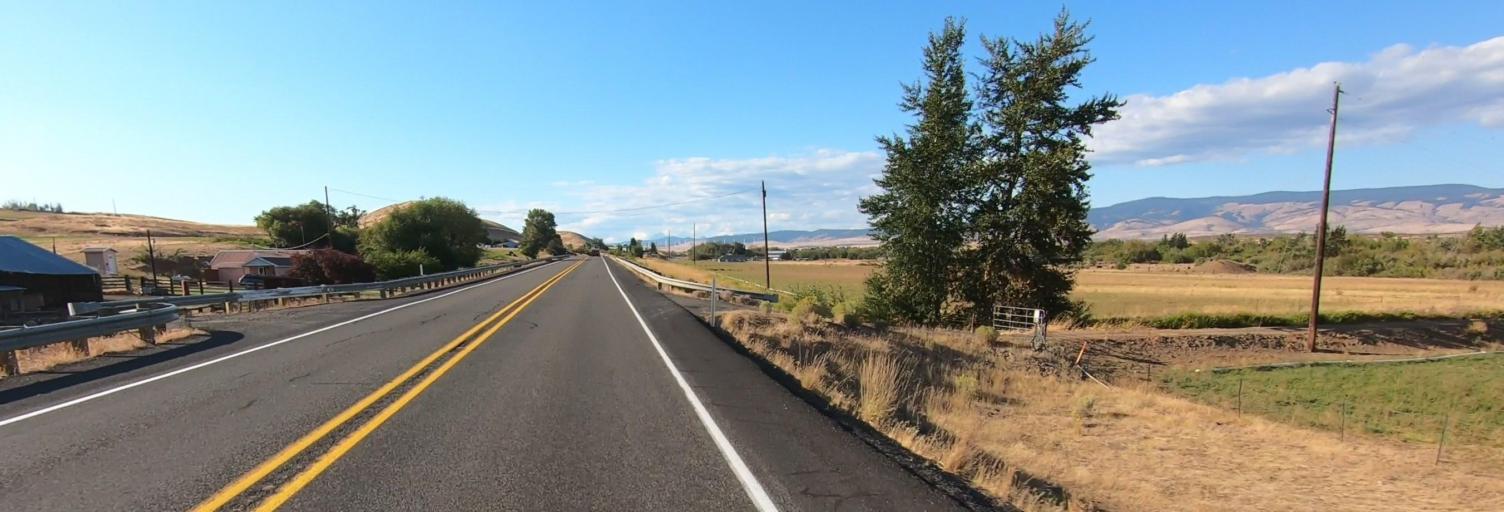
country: US
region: Washington
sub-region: Kittitas County
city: Ellensburg
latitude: 47.0584
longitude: -120.6178
